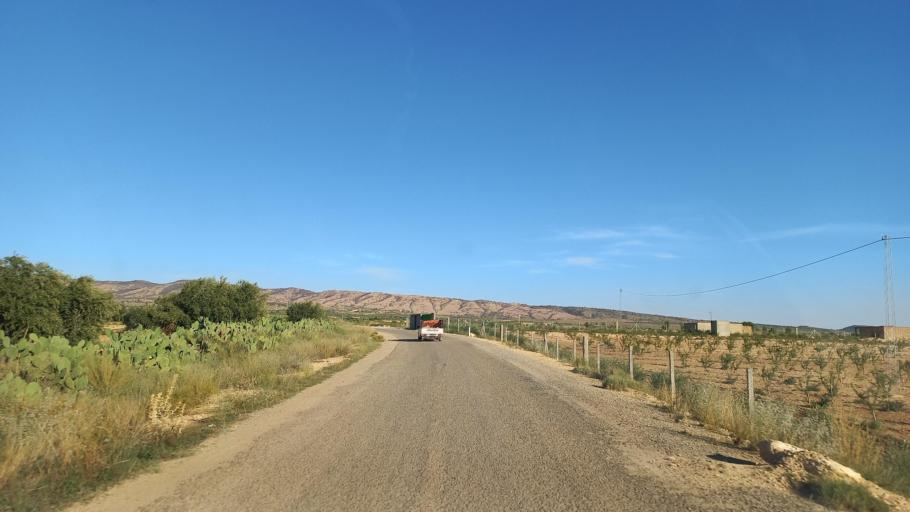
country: TN
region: Al Qasrayn
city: Sbiba
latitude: 35.3343
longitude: 9.0944
